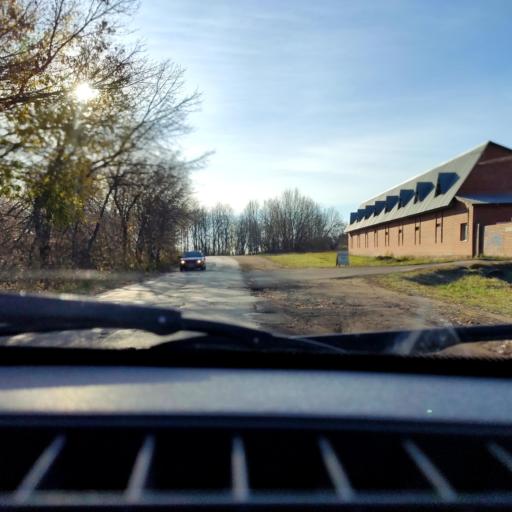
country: RU
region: Bashkortostan
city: Avdon
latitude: 54.7022
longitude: 55.8083
